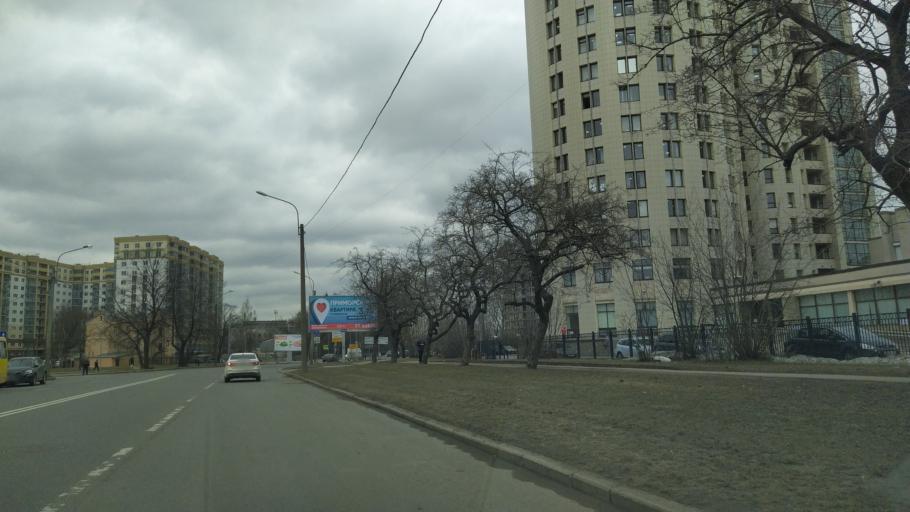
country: RU
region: St.-Petersburg
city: Centralniy
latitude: 59.9320
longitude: 30.4160
